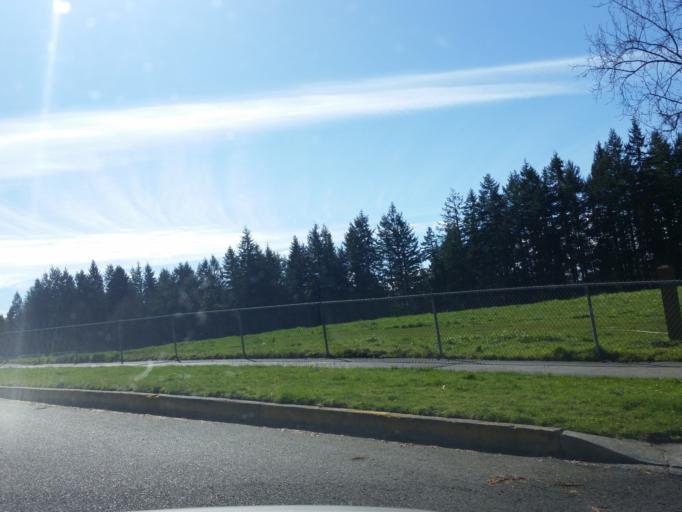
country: US
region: Washington
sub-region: Snohomish County
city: Esperance
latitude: 47.7886
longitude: -122.3700
